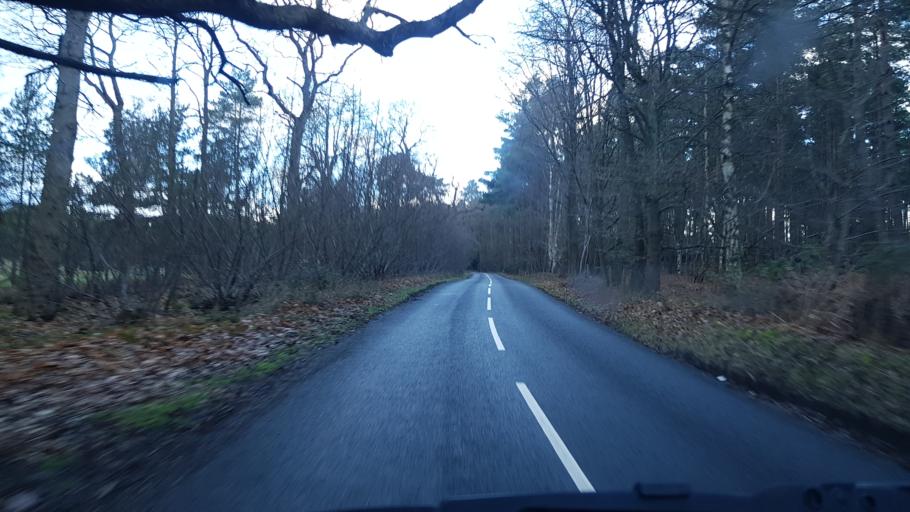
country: GB
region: England
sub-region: Surrey
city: Elstead
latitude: 51.2001
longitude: -0.7187
